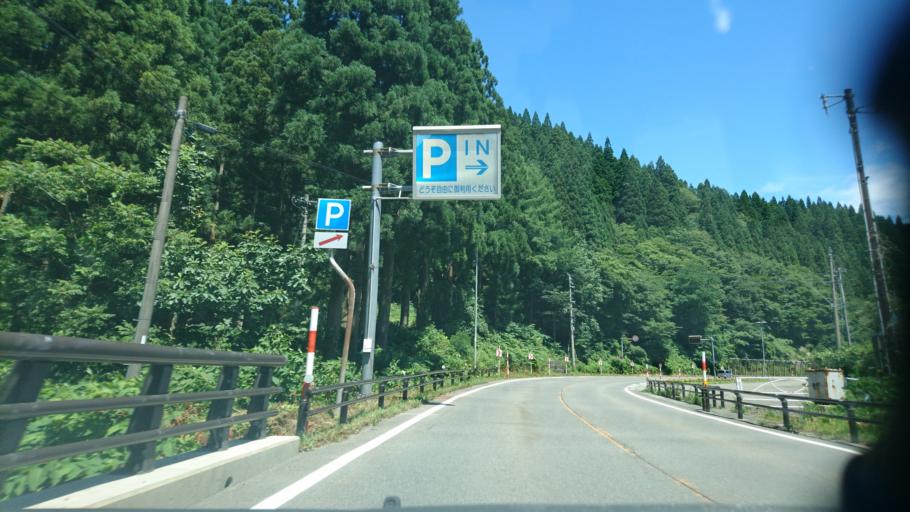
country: JP
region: Akita
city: Kakunodatemachi
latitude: 39.6417
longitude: 140.6605
